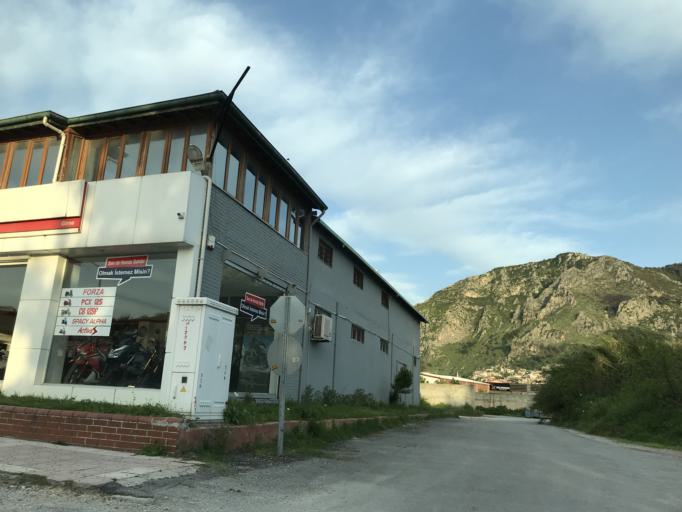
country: TR
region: Hatay
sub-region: Antakya Ilcesi
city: Antakya
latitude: 36.2118
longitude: 36.1671
